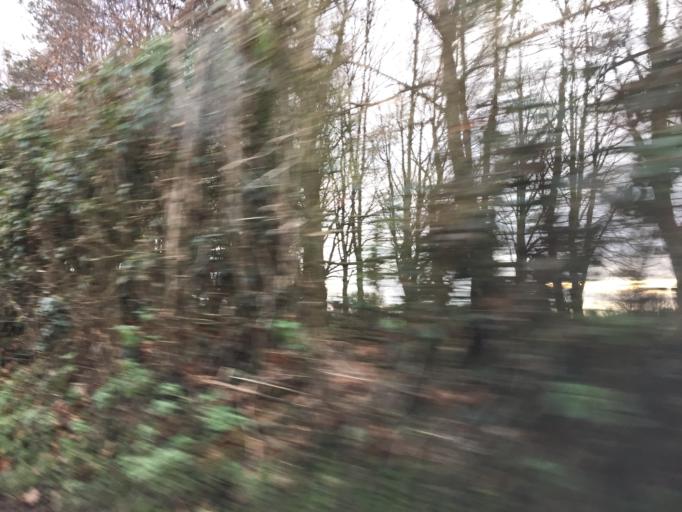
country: GB
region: Wales
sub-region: Monmouthshire
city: Rogiet
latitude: 51.5978
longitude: -2.7746
